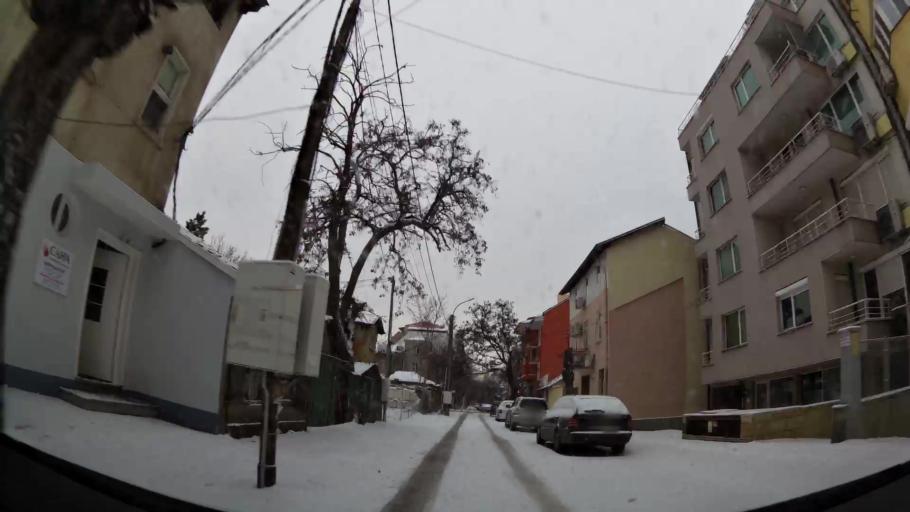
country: BG
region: Sofia-Capital
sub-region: Stolichna Obshtina
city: Sofia
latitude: 42.7013
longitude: 23.3065
